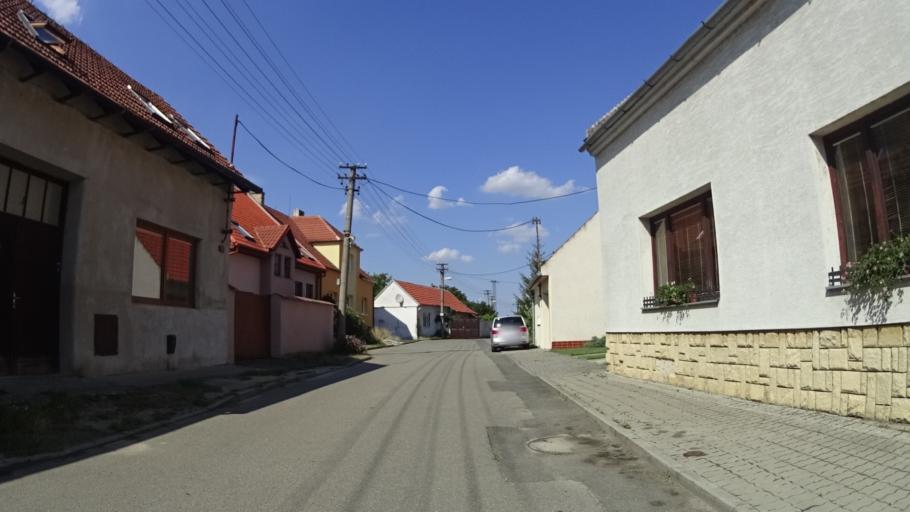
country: CZ
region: Zlin
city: Uhersky Ostroh
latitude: 48.9929
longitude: 17.4012
